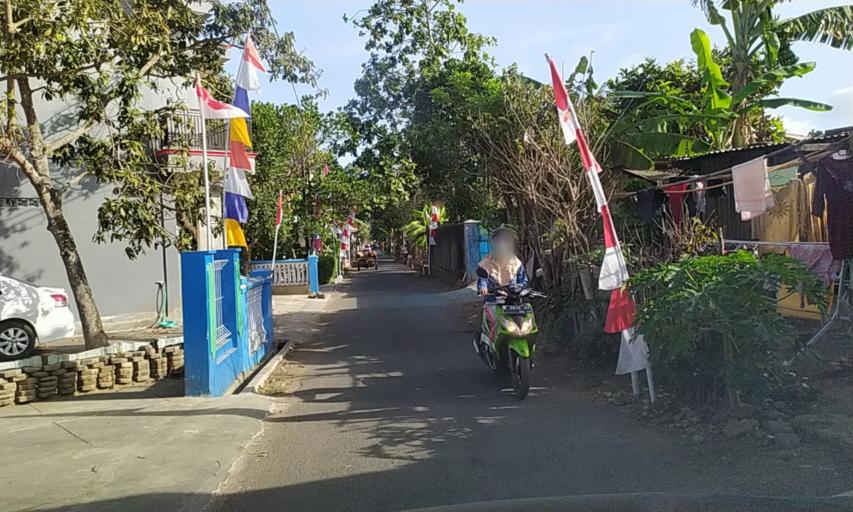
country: ID
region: Central Java
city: Rejanegara
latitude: -7.6752
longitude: 109.0289
